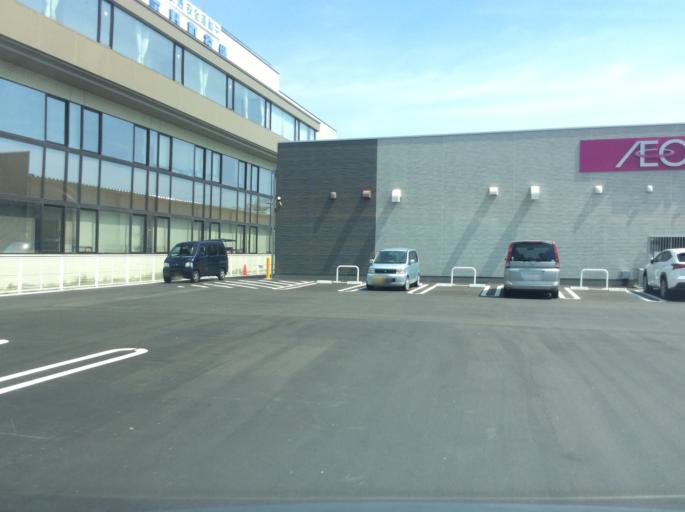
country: JP
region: Fukushima
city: Iwaki
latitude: 37.2140
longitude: 140.9944
